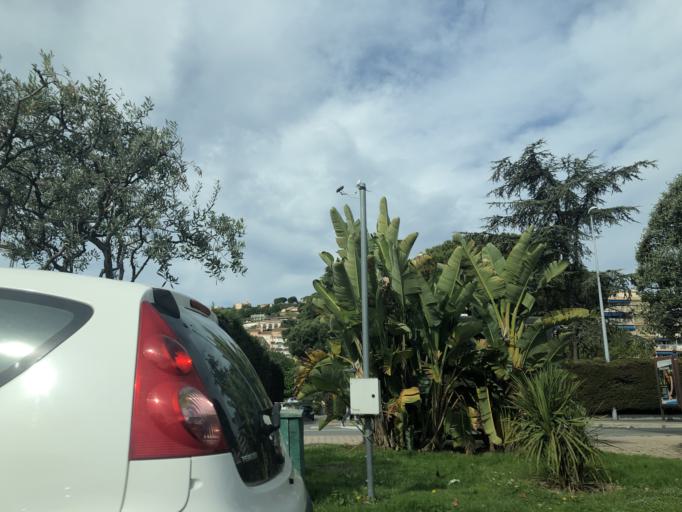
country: FR
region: Provence-Alpes-Cote d'Azur
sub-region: Departement des Alpes-Maritimes
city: Saint-Laurent-du-Var
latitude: 43.6805
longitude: 7.1900
